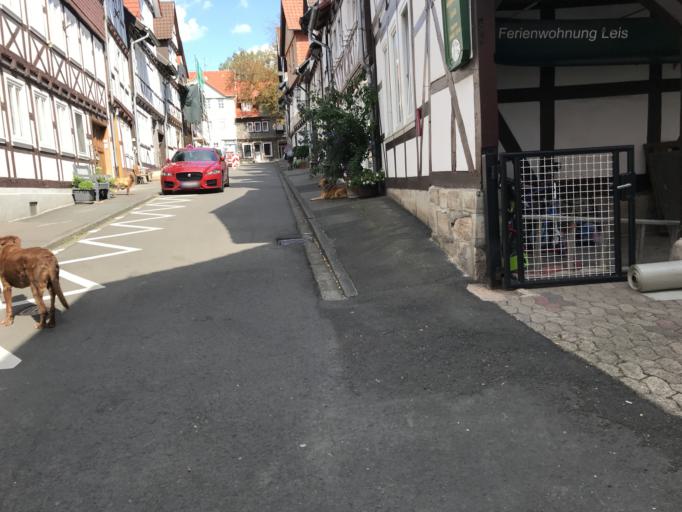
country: DE
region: Hesse
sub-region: Regierungsbezirk Kassel
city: Bad Sooden-Allendorf
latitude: 51.2712
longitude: 9.9756
